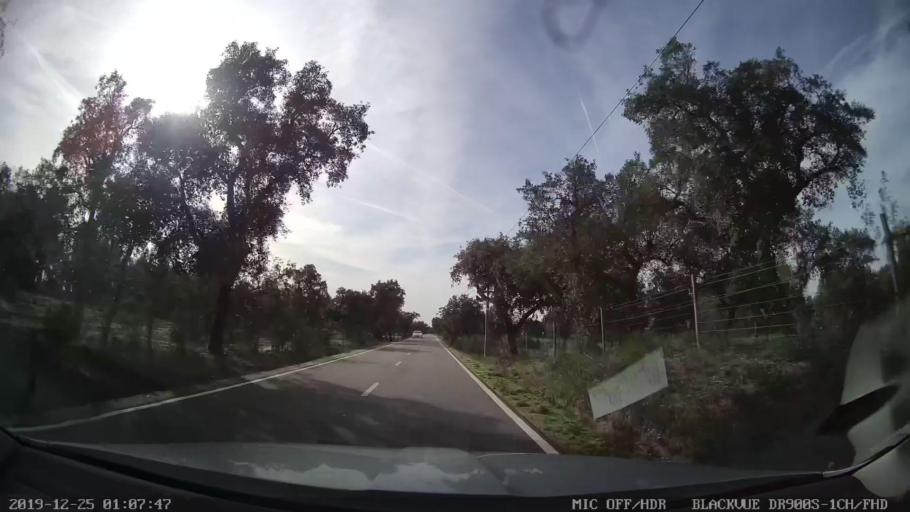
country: PT
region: Portalegre
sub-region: Nisa
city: Nisa
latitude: 39.4582
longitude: -7.7056
